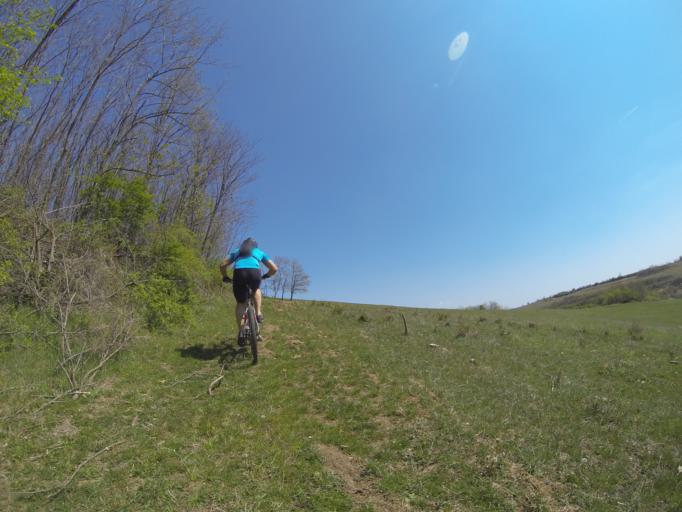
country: RO
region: Gorj
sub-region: Comuna Crusetu
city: Crusetu
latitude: 44.5868
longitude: 23.6596
